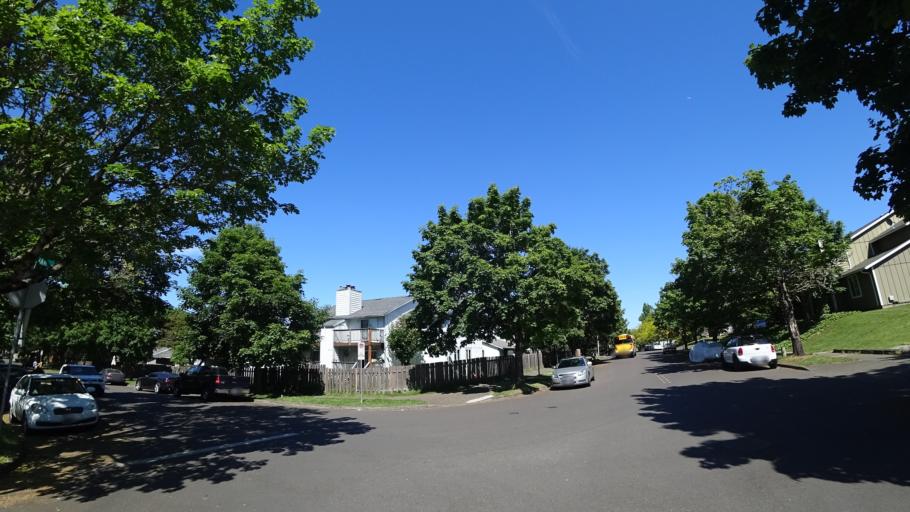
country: US
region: Oregon
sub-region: Washington County
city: Tigard
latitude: 45.4492
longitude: -122.8036
